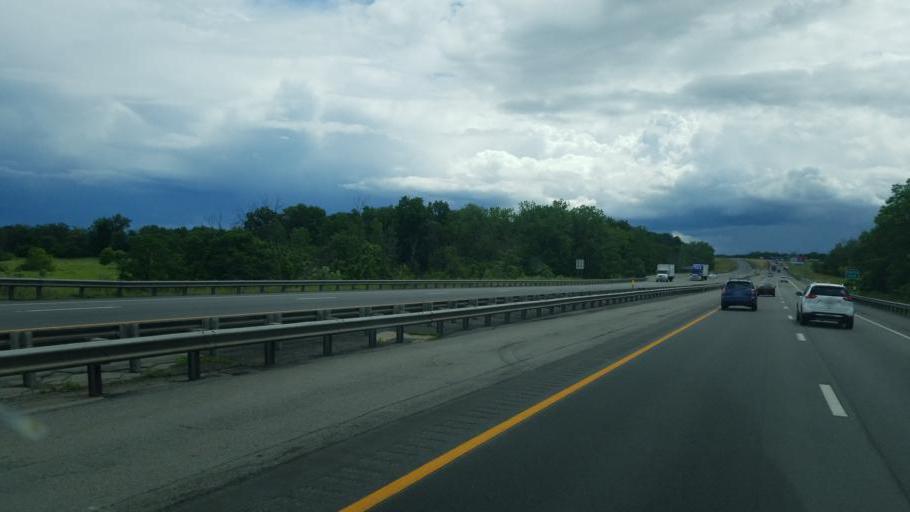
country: US
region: New York
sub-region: Monroe County
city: Scottsville
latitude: 43.0433
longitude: -77.7289
